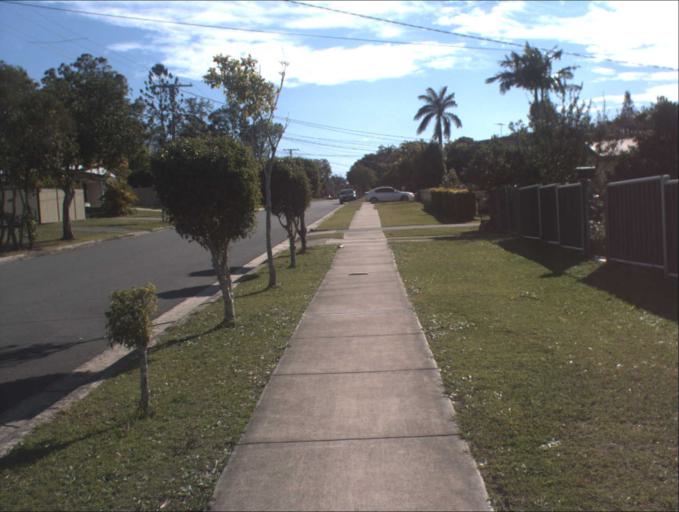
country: AU
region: Queensland
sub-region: Logan
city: Waterford West
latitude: -27.6804
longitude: 153.1059
